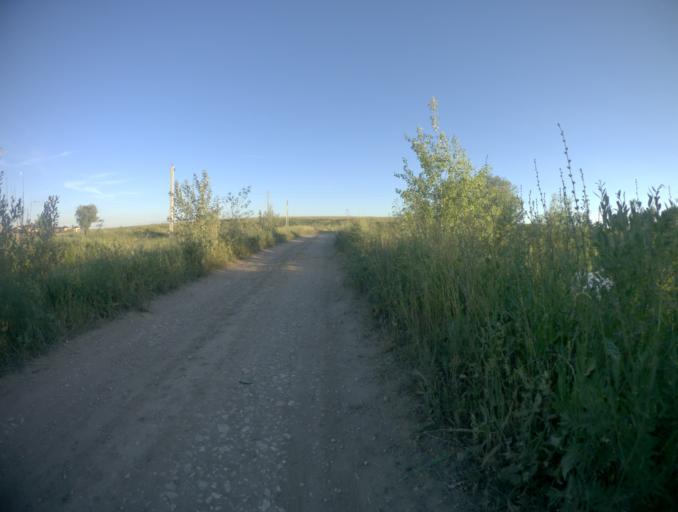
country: RU
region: Vladimir
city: Bogolyubovo
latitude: 56.2077
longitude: 40.5116
